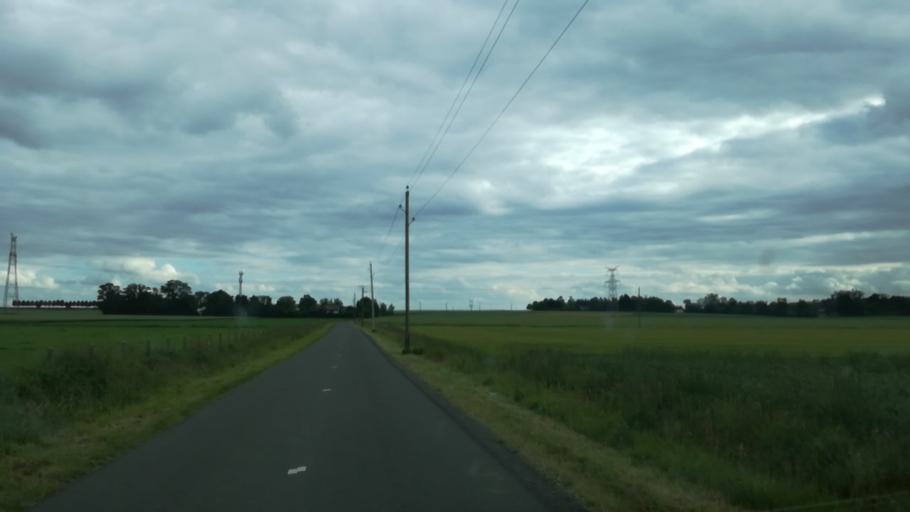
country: FR
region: Haute-Normandie
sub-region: Departement de l'Eure
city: Bourg-Achard
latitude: 49.3134
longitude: 0.8040
